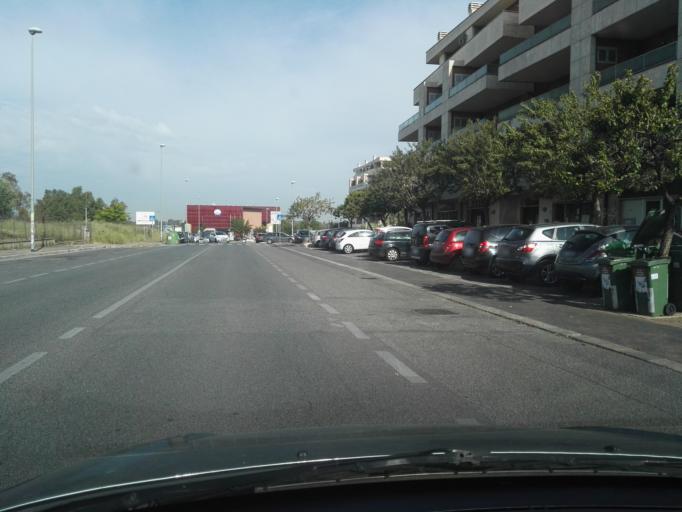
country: IT
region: Latium
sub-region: Citta metropolitana di Roma Capitale
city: Selcetta
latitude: 41.7663
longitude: 12.4719
